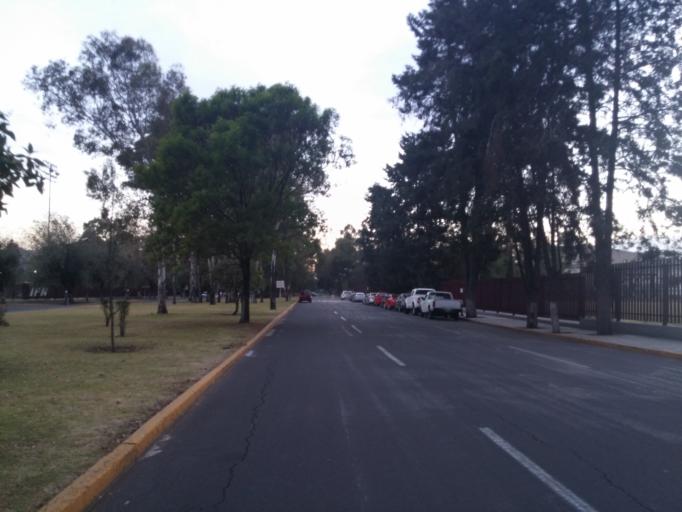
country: MX
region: Mexico
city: Colonia Lindavista
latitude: 19.5003
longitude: -99.1400
